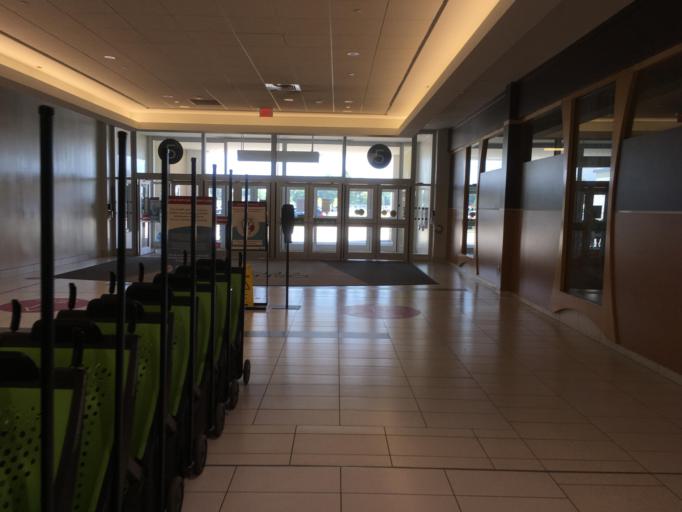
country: CA
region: Ontario
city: Oshawa
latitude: 43.8882
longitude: -78.8786
